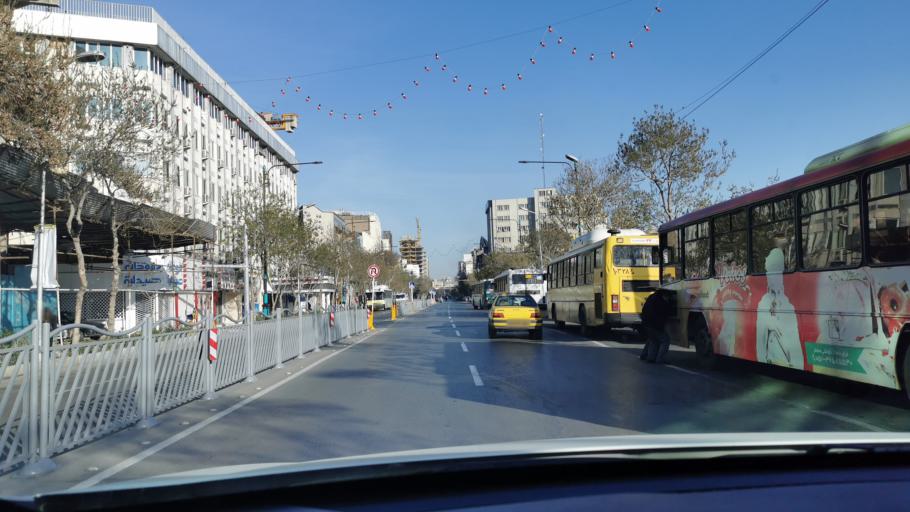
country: IR
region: Razavi Khorasan
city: Mashhad
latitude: 36.2849
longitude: 59.6114
